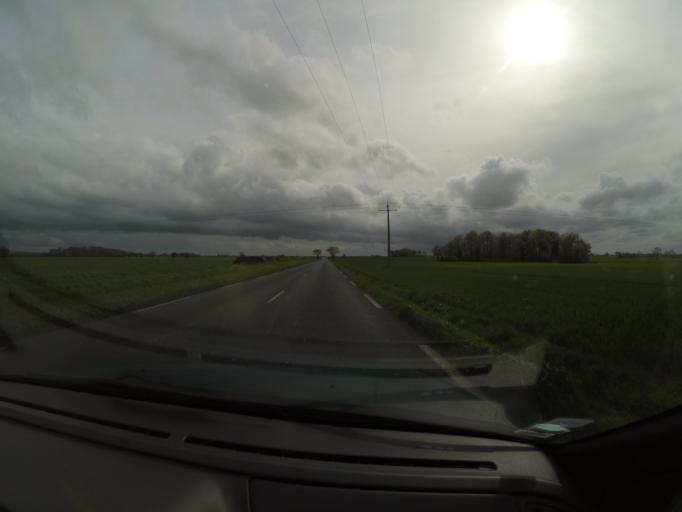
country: FR
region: Pays de la Loire
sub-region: Departement de Maine-et-Loire
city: Saint-Laurent-des-Autels
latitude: 47.2571
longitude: -1.2043
